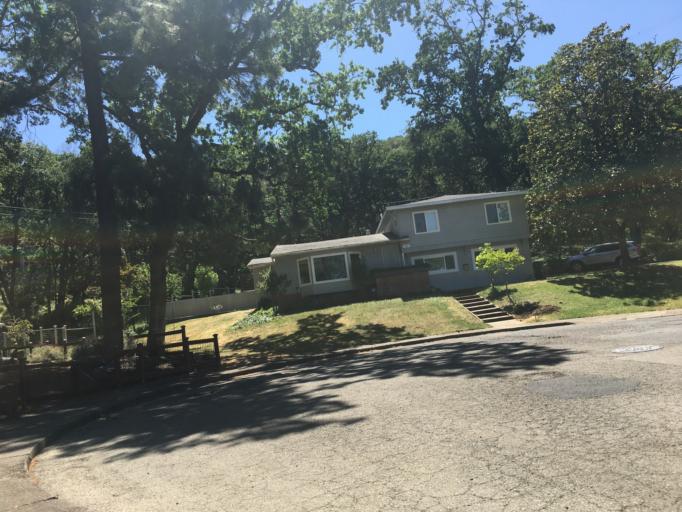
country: US
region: California
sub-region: Mendocino County
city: Ukiah
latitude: 39.1395
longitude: -123.2160
